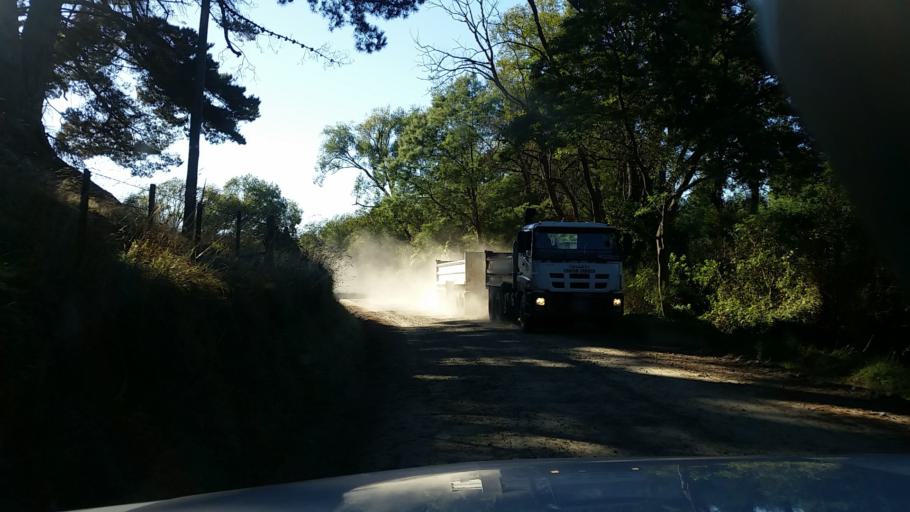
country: NZ
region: Marlborough
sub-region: Marlborough District
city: Blenheim
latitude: -41.4500
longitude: 173.8739
